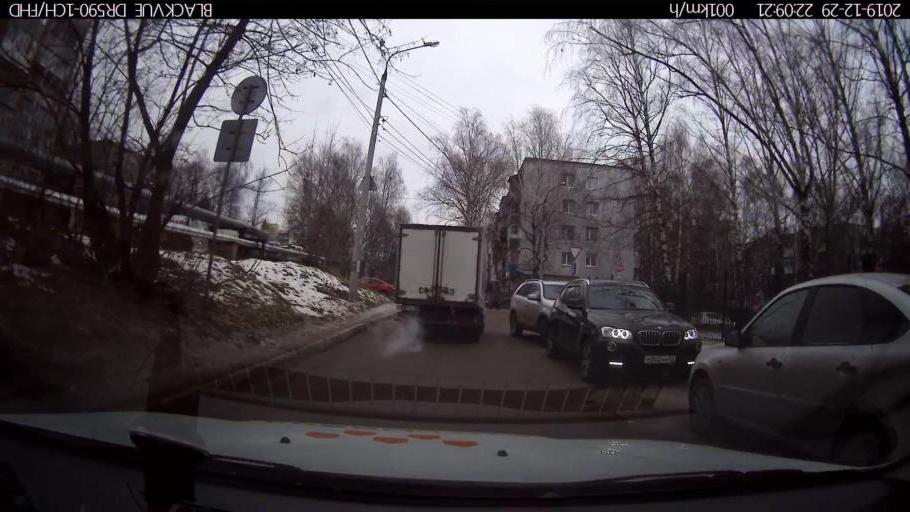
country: RU
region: Nizjnij Novgorod
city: Nizhniy Novgorod
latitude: 56.2318
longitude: 43.9530
